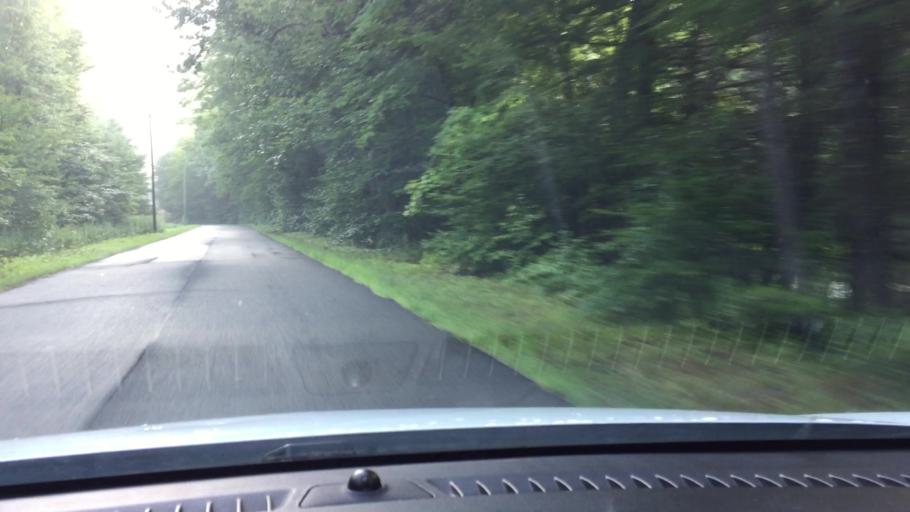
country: US
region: Massachusetts
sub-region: Berkshire County
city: Becket
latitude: 42.3666
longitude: -72.9683
